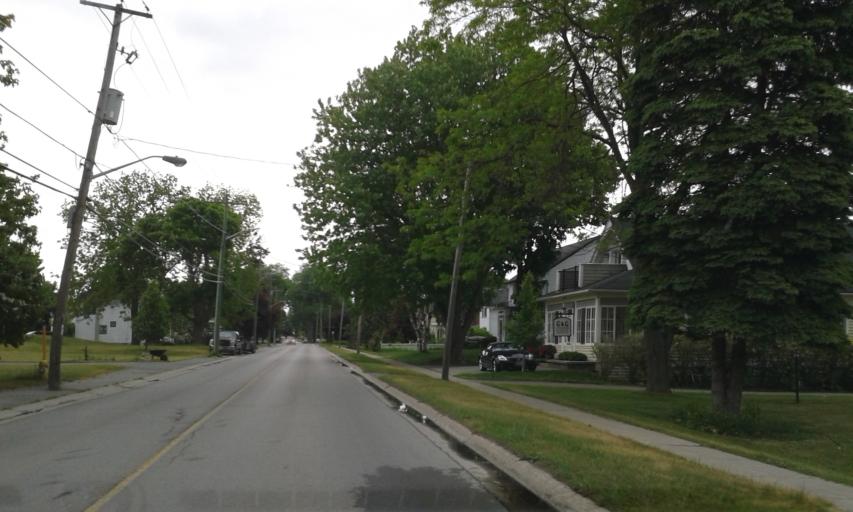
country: CA
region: Ontario
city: Prince Edward
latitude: 43.9501
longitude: -77.3593
